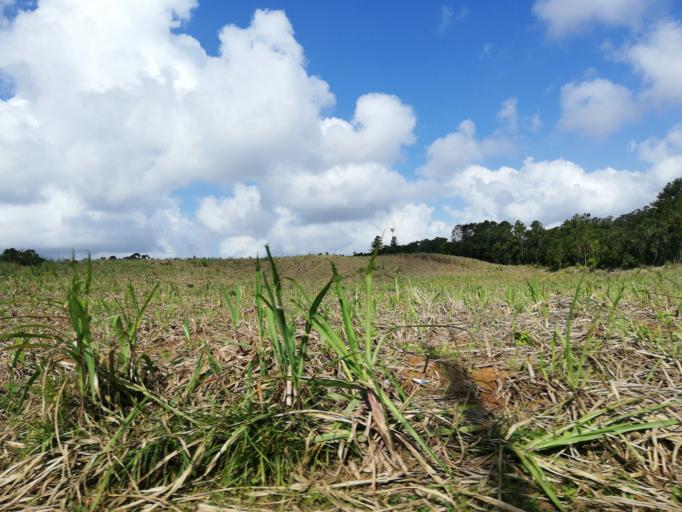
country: MU
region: Pamplemousses
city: Creve Coeur
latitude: -20.2049
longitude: 57.5591
